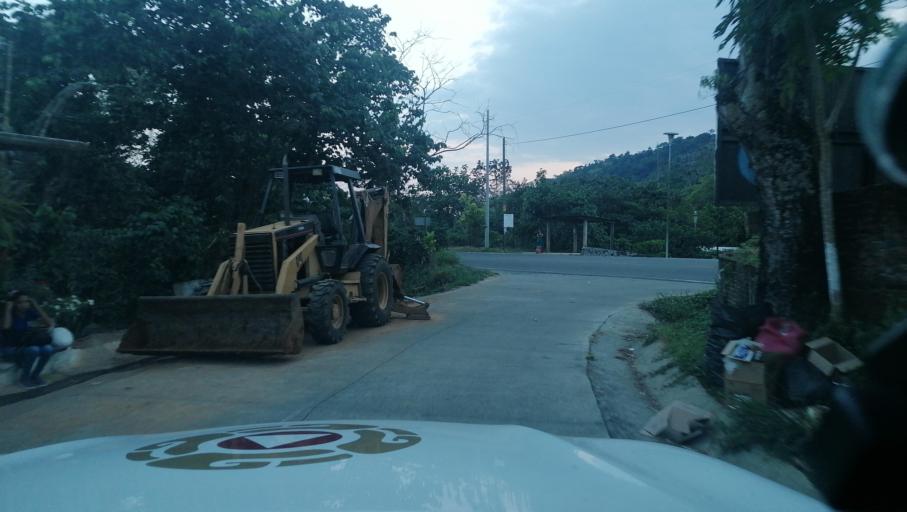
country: MX
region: Chiapas
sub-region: Cacahoatan
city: Benito Juarez
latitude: 15.0512
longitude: -92.2436
